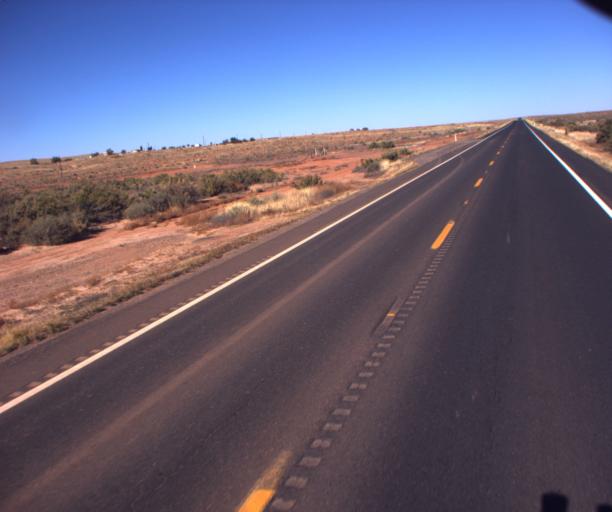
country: US
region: Arizona
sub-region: Coconino County
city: Kaibito
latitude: 36.3418
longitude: -110.9166
